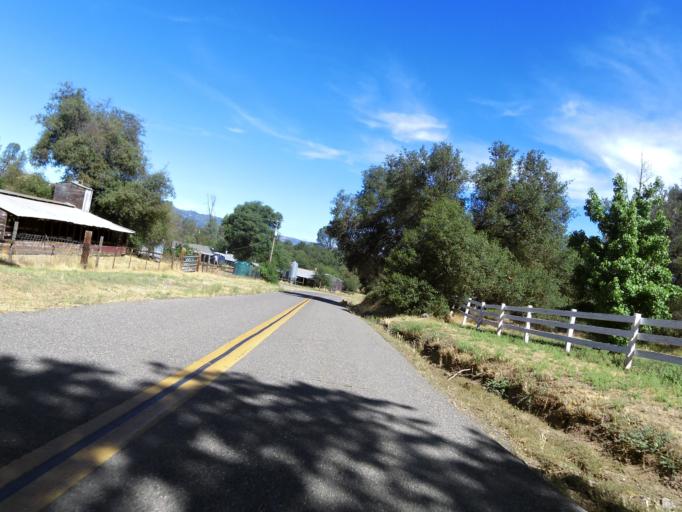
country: US
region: California
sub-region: Mariposa County
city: Mariposa
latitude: 37.4188
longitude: -119.9651
